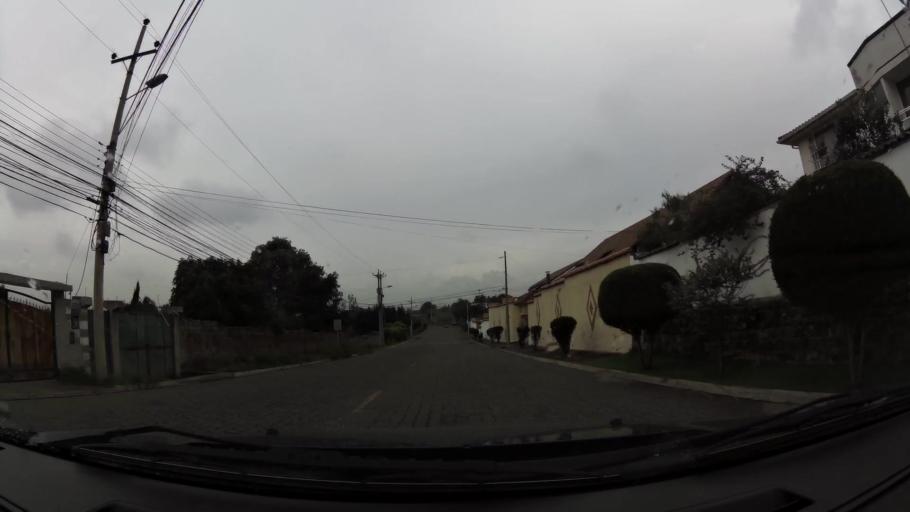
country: EC
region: Pichincha
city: Sangolqui
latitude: -0.2851
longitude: -78.4670
